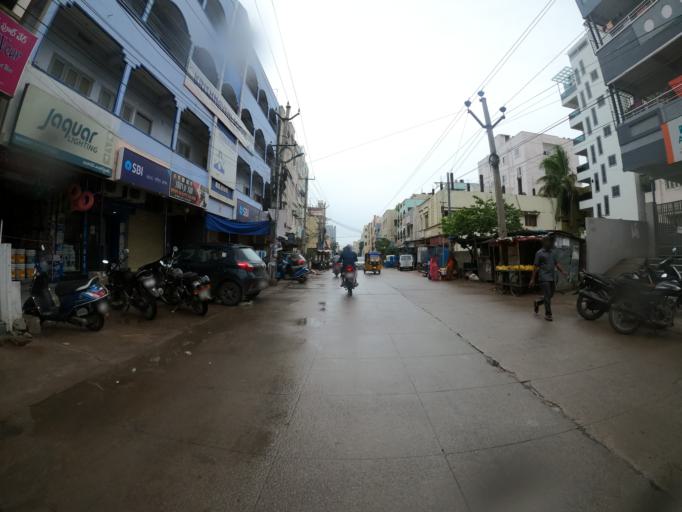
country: IN
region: Telangana
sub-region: Rangareddi
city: Kukatpalli
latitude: 17.4586
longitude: 78.4024
